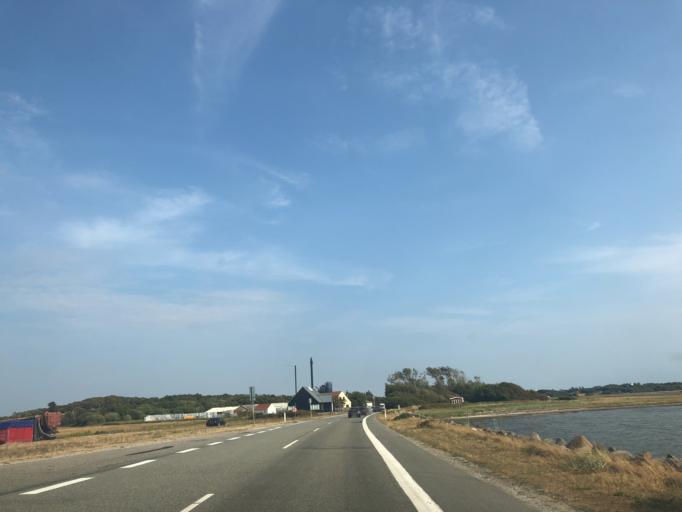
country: DK
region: North Denmark
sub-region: Morso Kommune
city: Nykobing Mors
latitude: 56.7995
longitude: 9.0275
